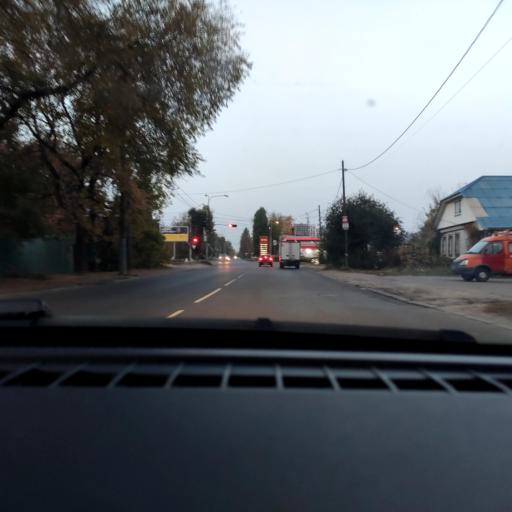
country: RU
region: Voronezj
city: Voronezh
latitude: 51.6658
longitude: 39.1774
